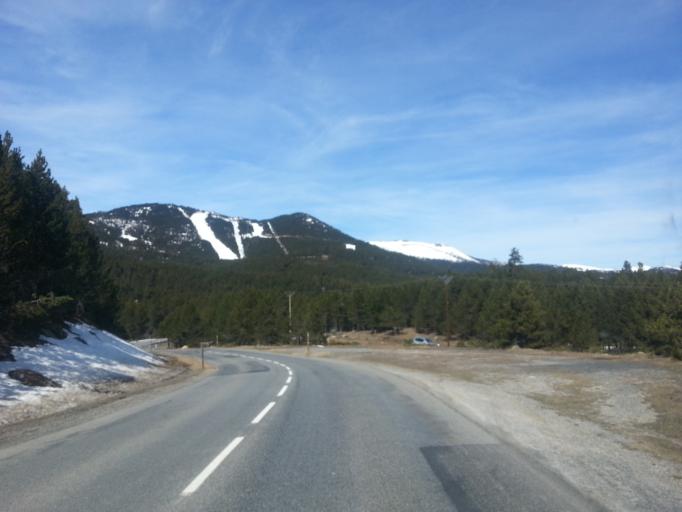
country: ES
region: Catalonia
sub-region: Provincia de Girona
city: Llivia
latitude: 42.5555
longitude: 2.0799
